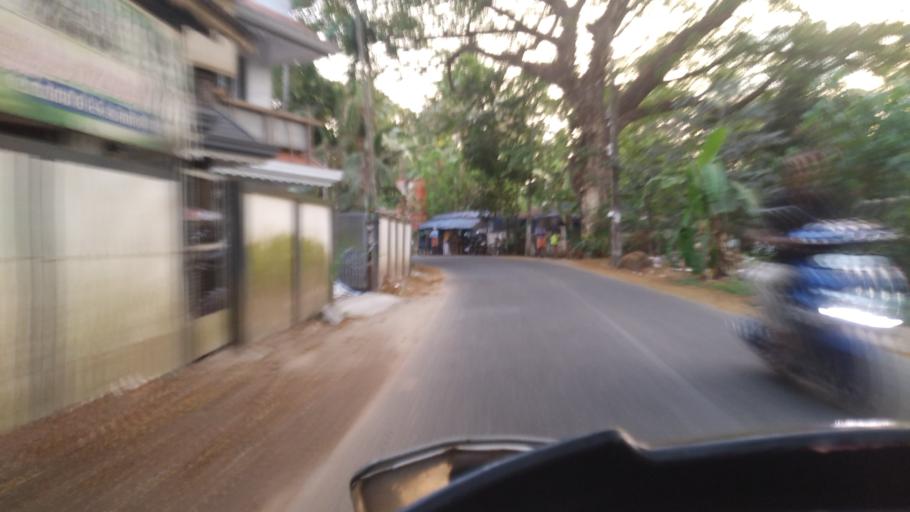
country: IN
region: Kerala
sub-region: Thrissur District
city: Kodungallur
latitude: 10.1763
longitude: 76.1995
